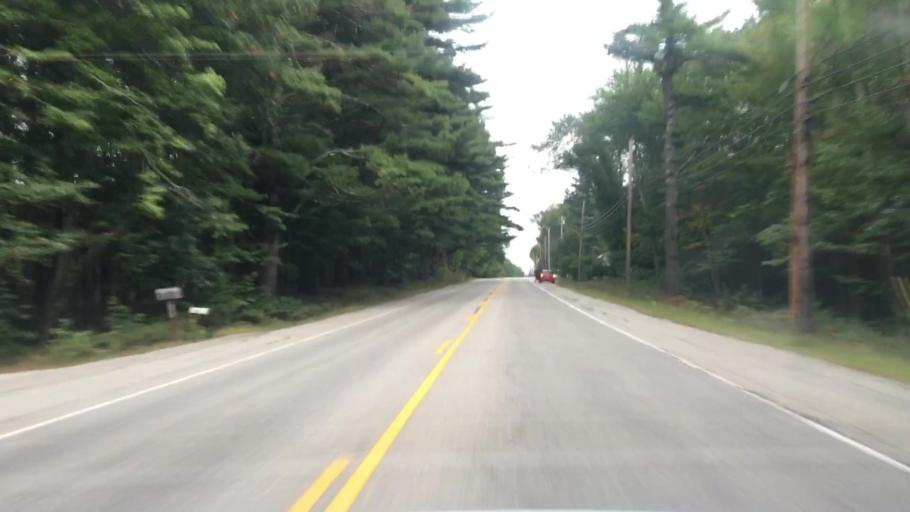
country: US
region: Maine
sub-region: York County
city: Alfred
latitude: 43.4763
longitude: -70.6836
